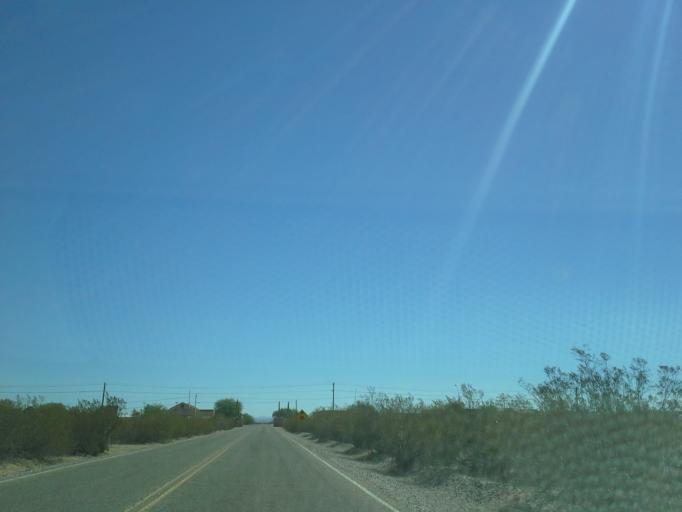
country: US
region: Arizona
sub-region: Pinal County
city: Coolidge
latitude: 32.9954
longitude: -111.5264
